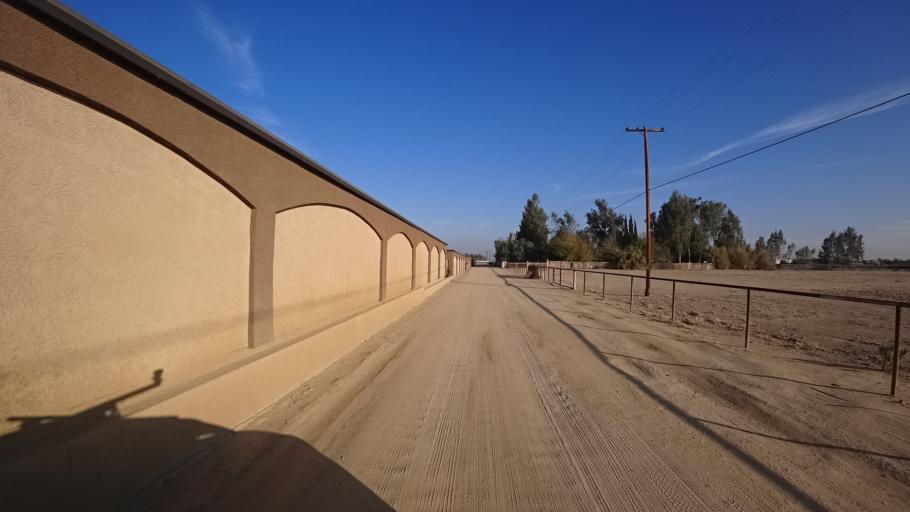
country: US
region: California
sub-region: Kern County
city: Greenacres
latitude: 35.4280
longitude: -119.1235
